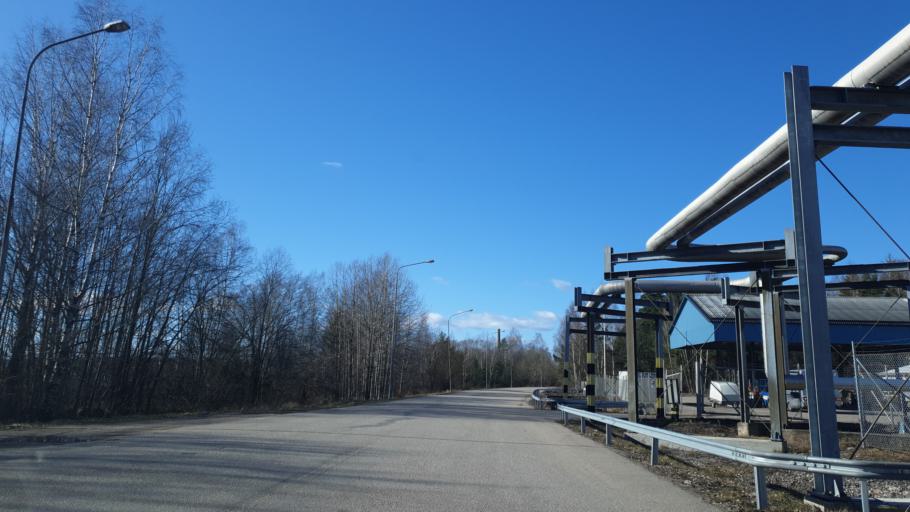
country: SE
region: Vaestmanland
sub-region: Kopings Kommun
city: Koping
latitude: 59.4951
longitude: 16.0446
